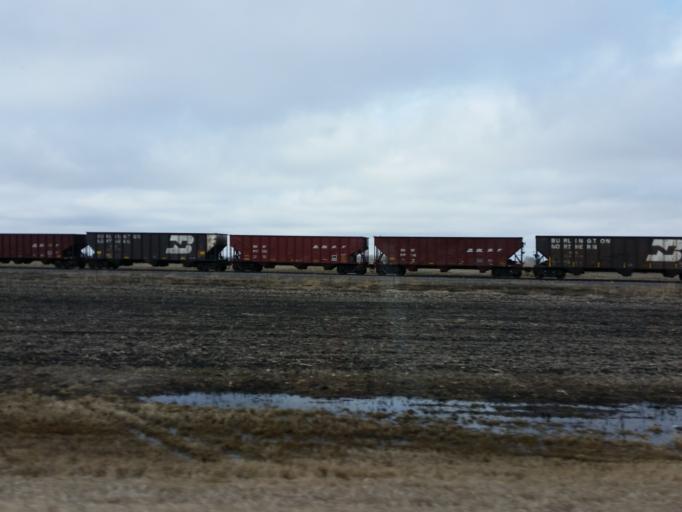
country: US
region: North Dakota
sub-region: Cass County
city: Casselton
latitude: 47.0426
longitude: -97.2179
